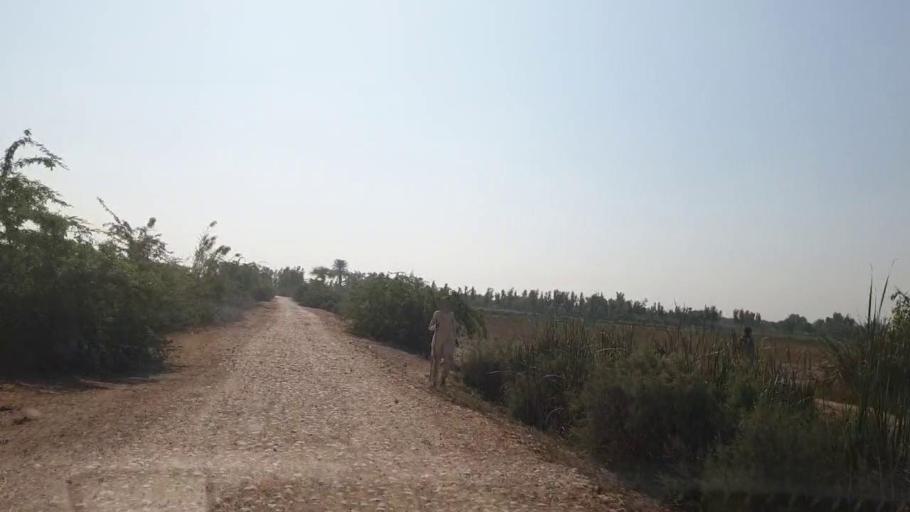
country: PK
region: Sindh
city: Gharo
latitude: 24.6809
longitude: 67.7496
